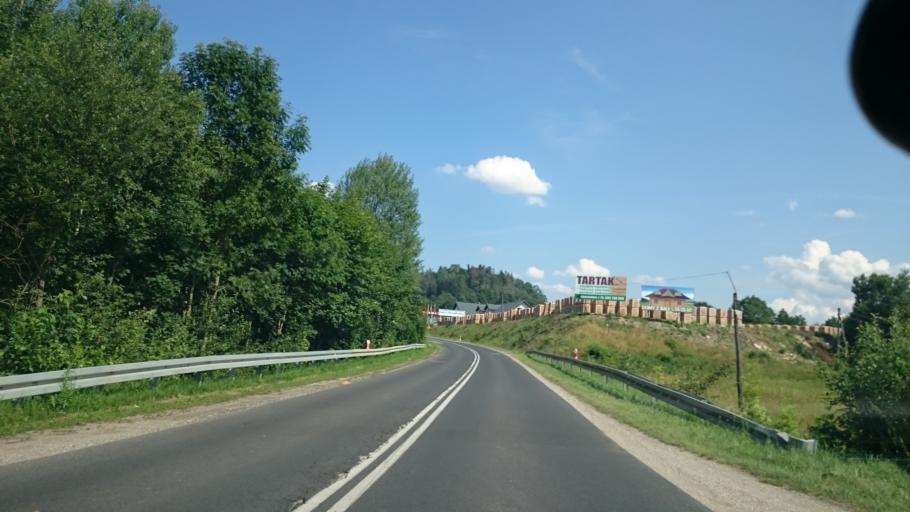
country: PL
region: Lower Silesian Voivodeship
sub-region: Powiat klodzki
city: Ladek-Zdroj
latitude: 50.3393
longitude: 16.8051
